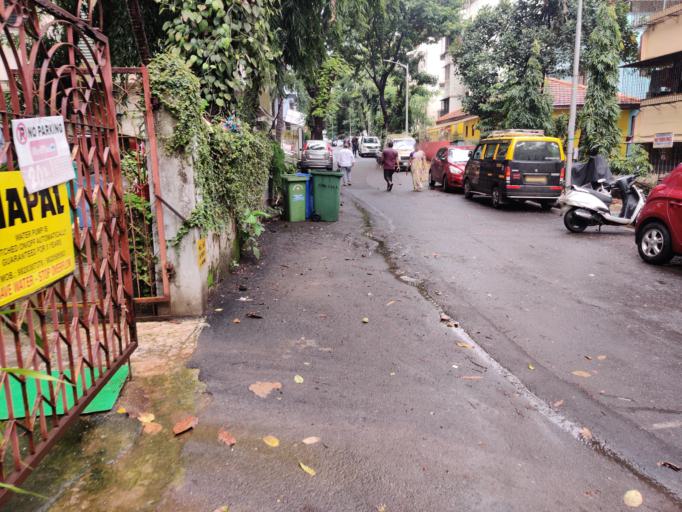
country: IN
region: Maharashtra
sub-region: Mumbai Suburban
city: Borivli
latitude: 19.2474
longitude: 72.8539
